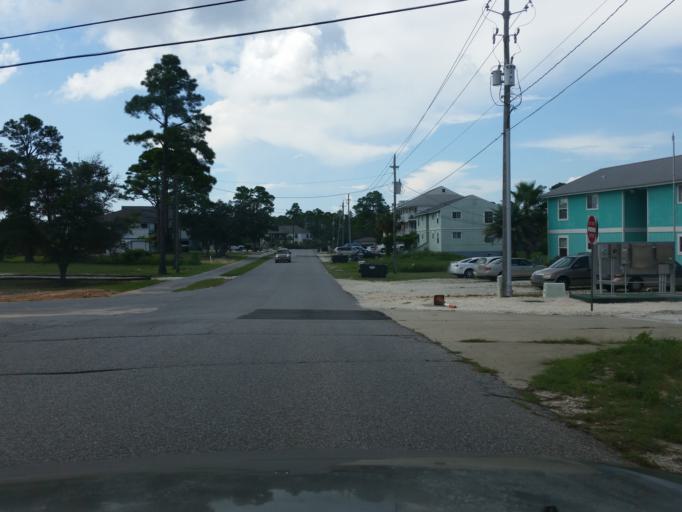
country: US
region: Alabama
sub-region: Baldwin County
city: Orange Beach
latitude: 30.3103
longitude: -87.4265
